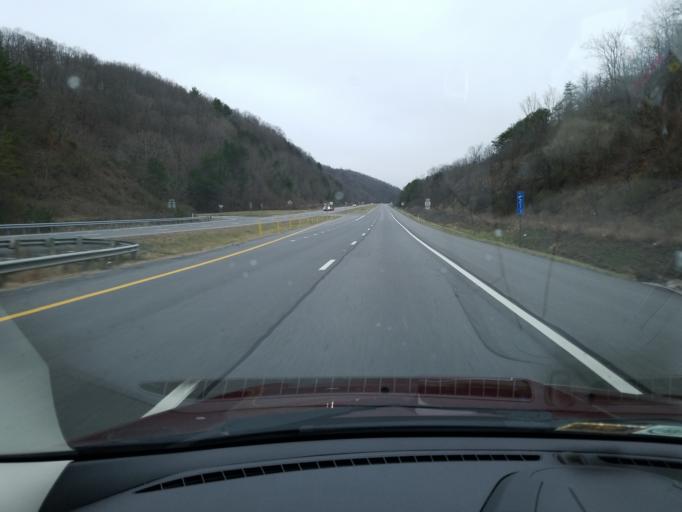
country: US
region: West Virginia
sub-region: Mercer County
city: Athens
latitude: 37.3431
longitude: -80.9569
